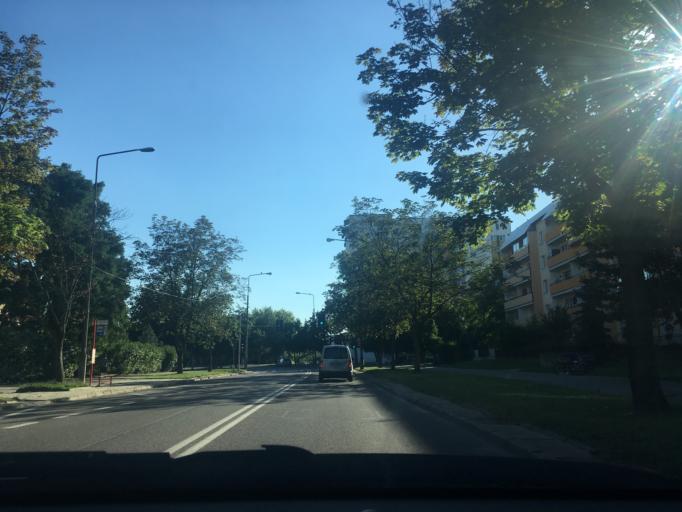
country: PL
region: Podlasie
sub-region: Bialystok
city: Bialystok
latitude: 53.1444
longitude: 23.1502
